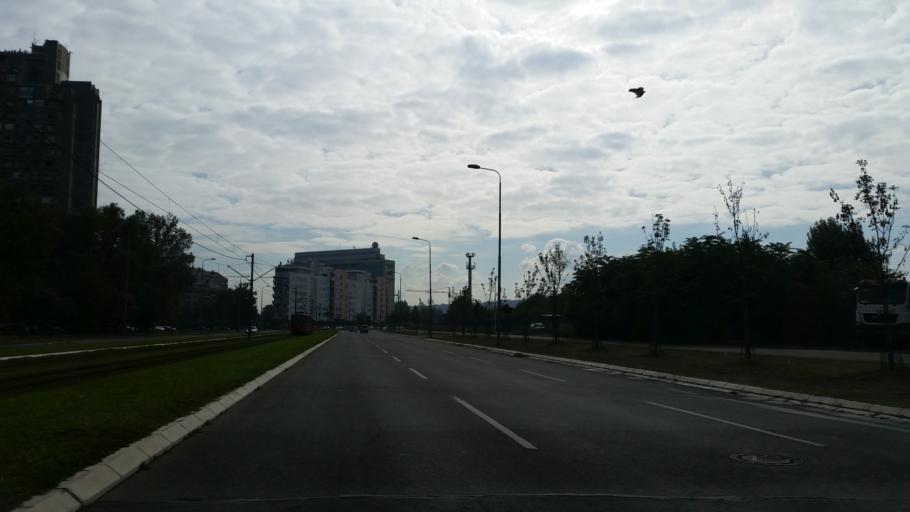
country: RS
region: Central Serbia
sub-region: Belgrade
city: Novi Beograd
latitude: 44.8066
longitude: 20.4230
